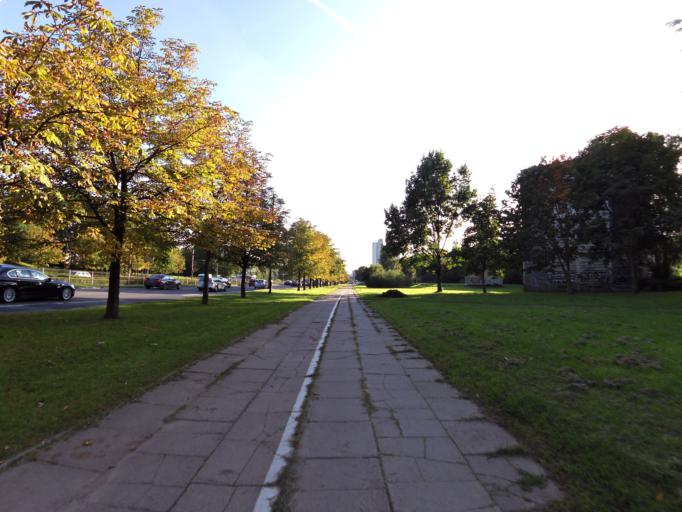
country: LT
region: Vilnius County
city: Justiniskes
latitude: 54.7055
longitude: 25.2256
